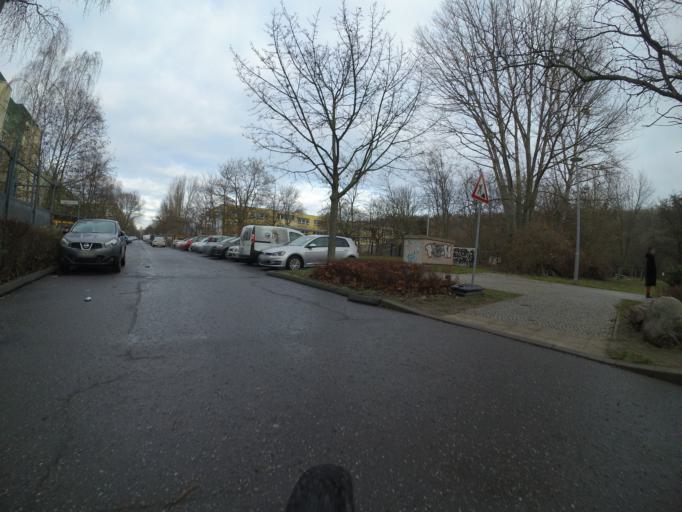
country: DE
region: Berlin
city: Marzahn
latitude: 52.5519
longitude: 13.5789
